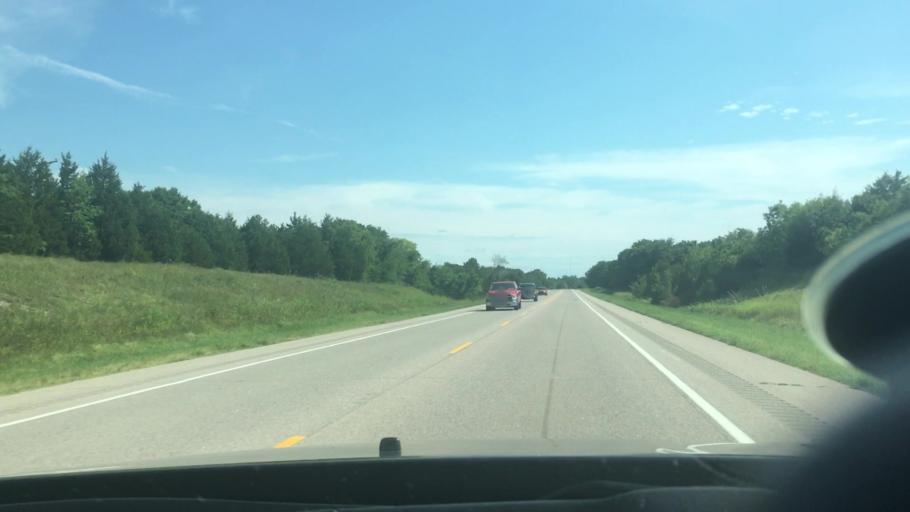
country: US
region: Oklahoma
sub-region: Seminole County
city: Konawa
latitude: 34.9640
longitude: -96.6788
